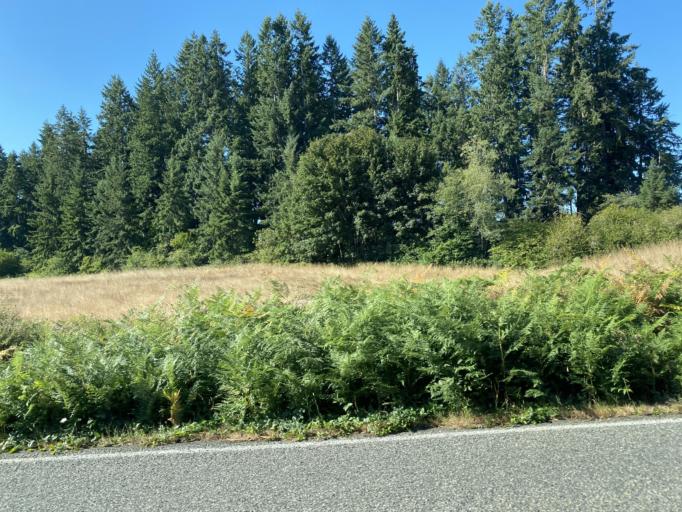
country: US
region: Washington
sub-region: Thurston County
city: Rainier
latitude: 46.9001
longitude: -122.7566
